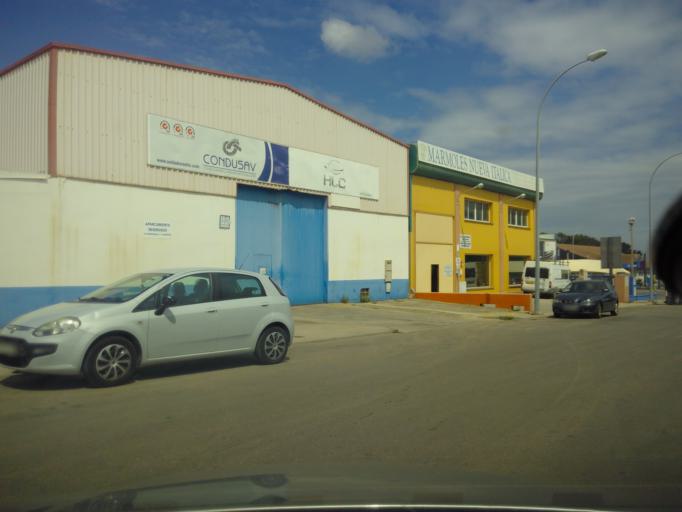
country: ES
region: Andalusia
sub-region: Provincia de Cadiz
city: La Linea de la Concepcion
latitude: 36.1836
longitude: -5.3508
